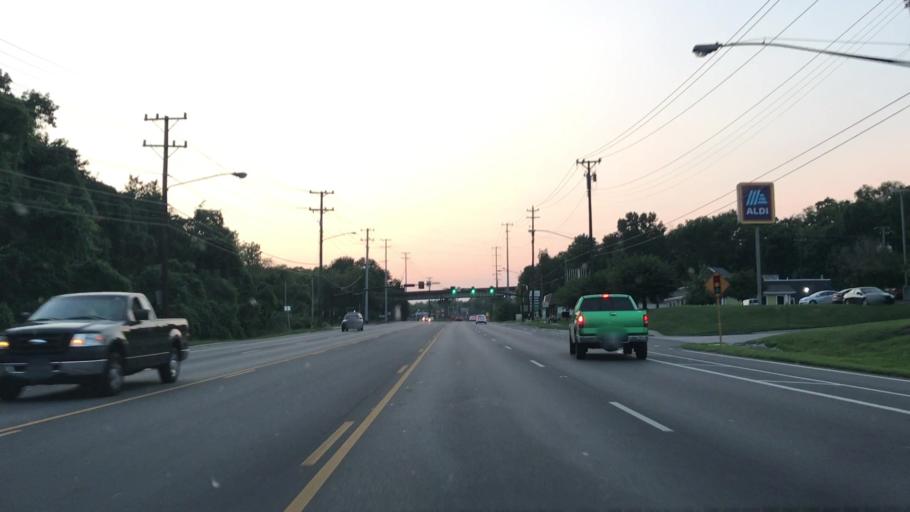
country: US
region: Tennessee
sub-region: Davidson County
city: Oak Hill
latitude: 36.0890
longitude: -86.7325
